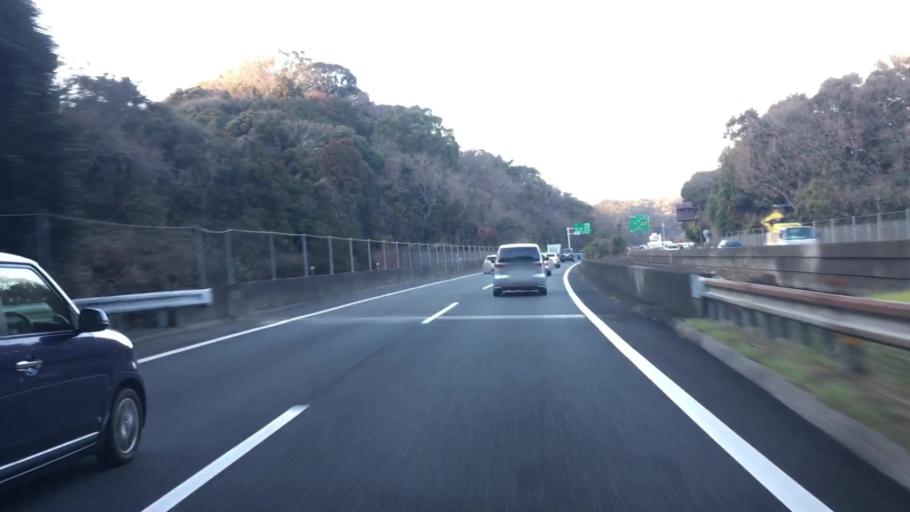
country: JP
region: Kanagawa
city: Zushi
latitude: 35.3278
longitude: 139.5952
